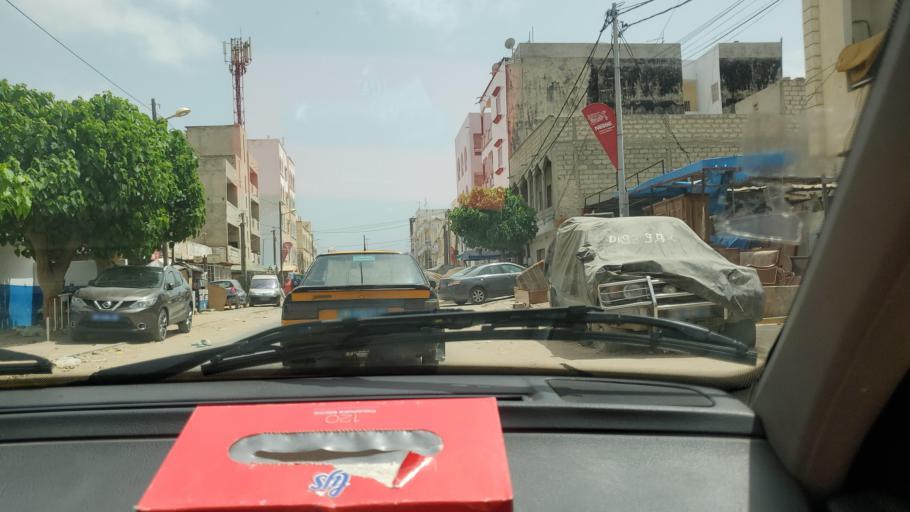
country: SN
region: Dakar
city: Grand Dakar
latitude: 14.7410
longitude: -17.4566
